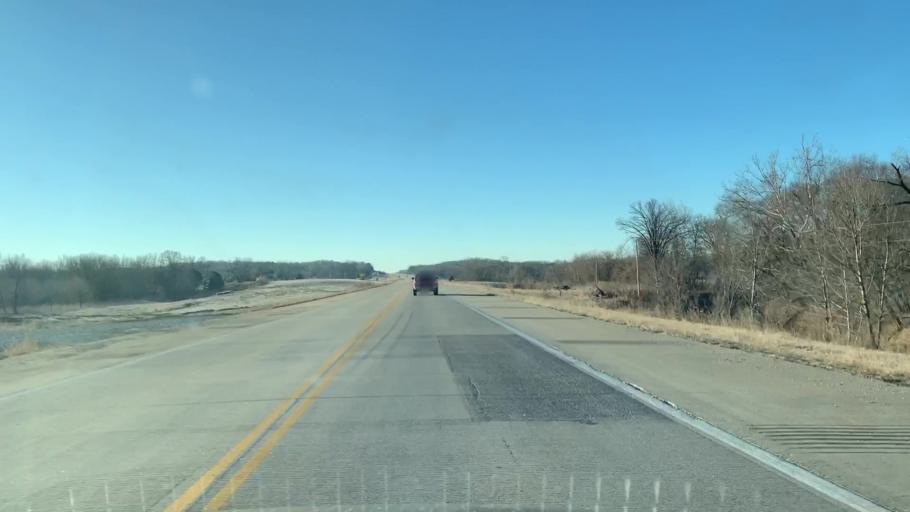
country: US
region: Kansas
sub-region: Crawford County
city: Arma
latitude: 37.6759
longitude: -94.7035
